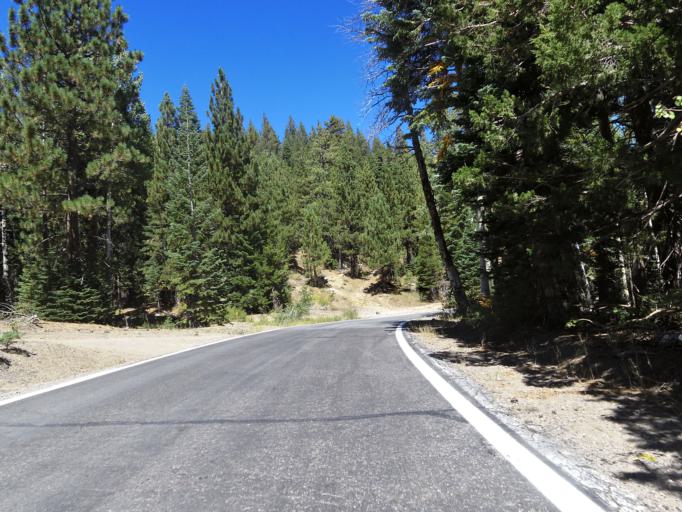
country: US
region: Nevada
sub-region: Douglas County
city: Gardnerville Ranchos
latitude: 38.5787
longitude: -119.8074
